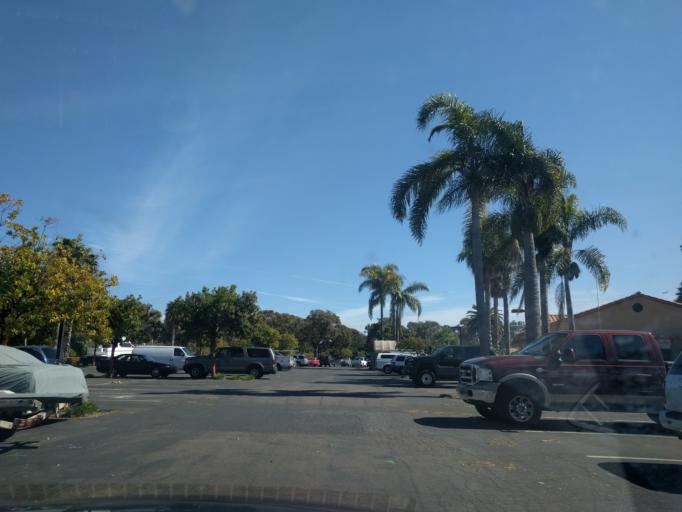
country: US
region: California
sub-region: San Diego County
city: La Jolla
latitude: 32.7642
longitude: -117.2369
